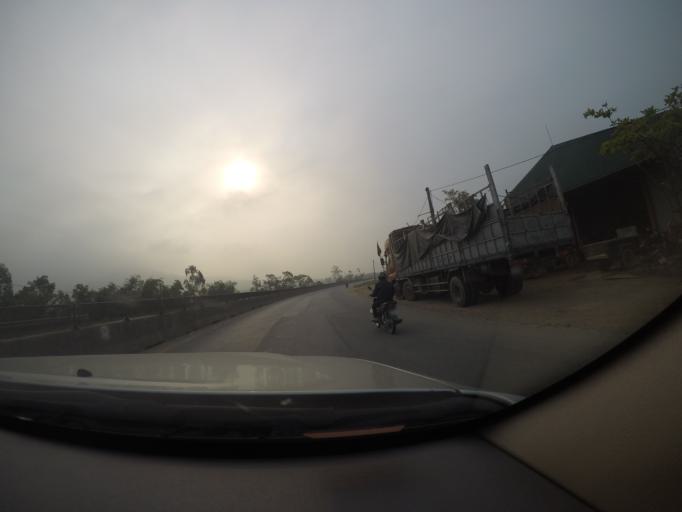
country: VN
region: Ha Tinh
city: Cam Xuyen
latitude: 18.2114
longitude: 106.1154
